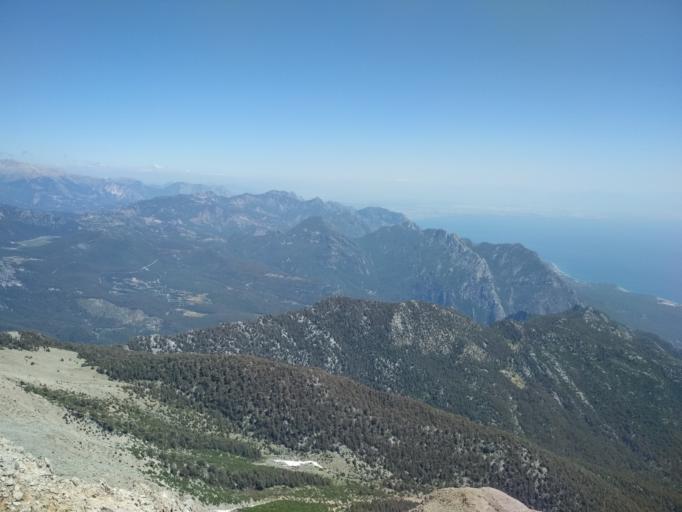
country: TR
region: Antalya
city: Tekirova
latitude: 36.5367
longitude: 30.4420
